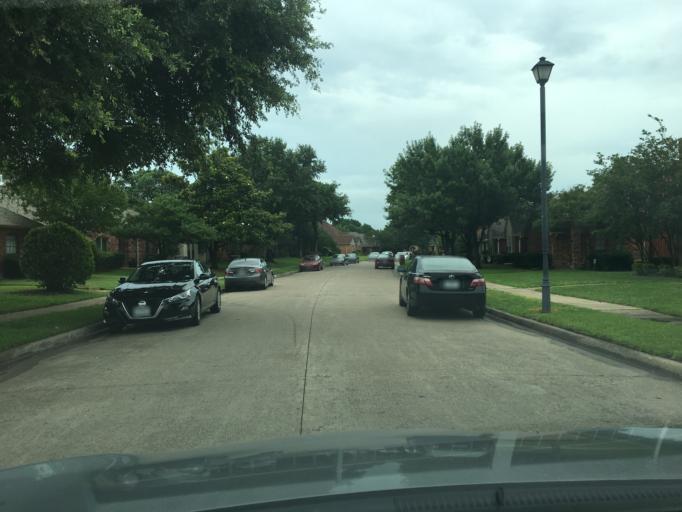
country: US
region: Texas
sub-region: Dallas County
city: Garland
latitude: 32.9414
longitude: -96.6708
